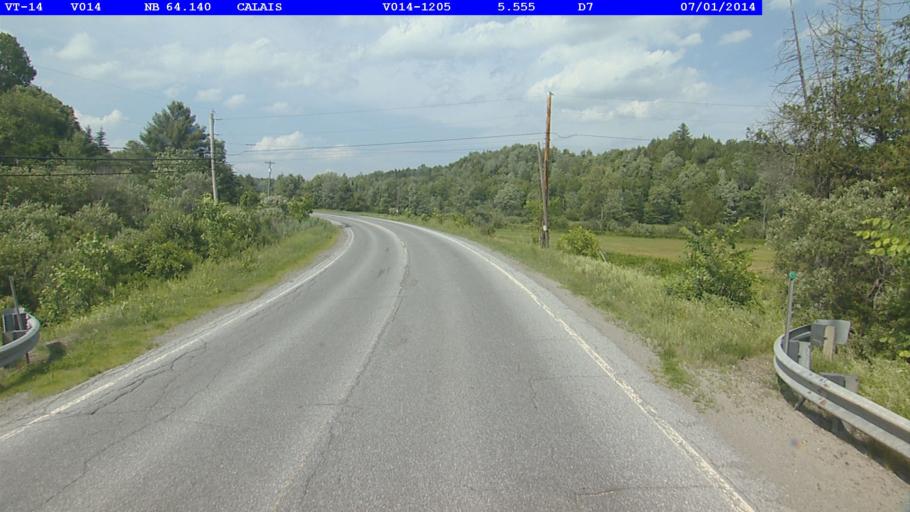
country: US
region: Vermont
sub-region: Caledonia County
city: Hardwick
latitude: 44.3774
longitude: -72.4186
